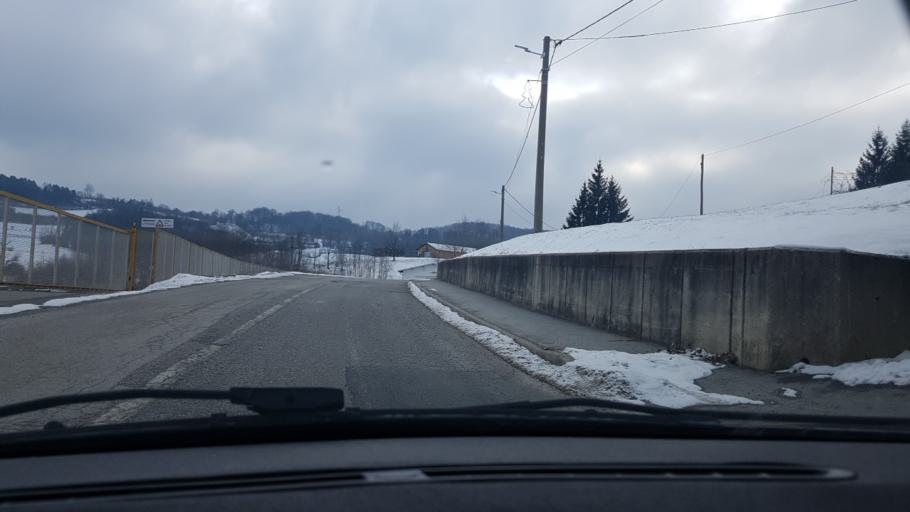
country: HR
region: Krapinsko-Zagorska
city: Mihovljan
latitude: 46.1733
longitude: 15.9828
